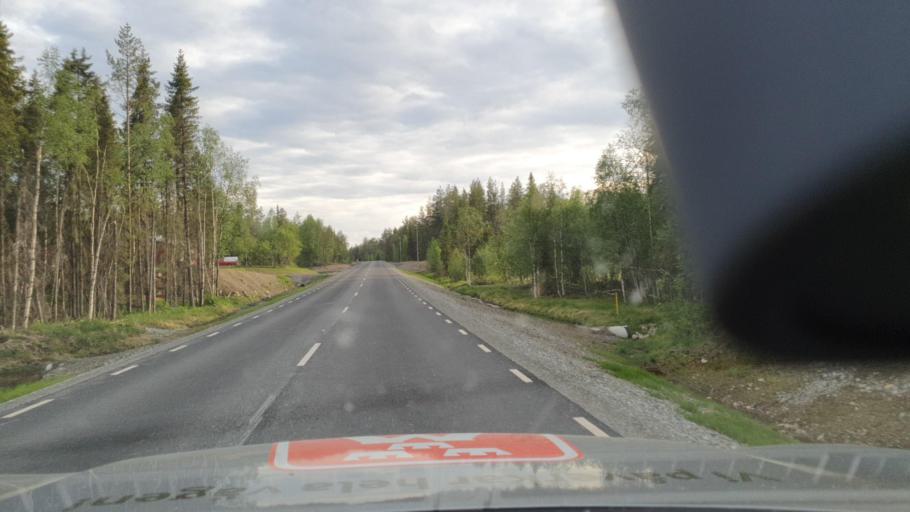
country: SE
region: Norrbotten
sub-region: Gallivare Kommun
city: Gaellivare
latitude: 66.8835
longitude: 21.2648
